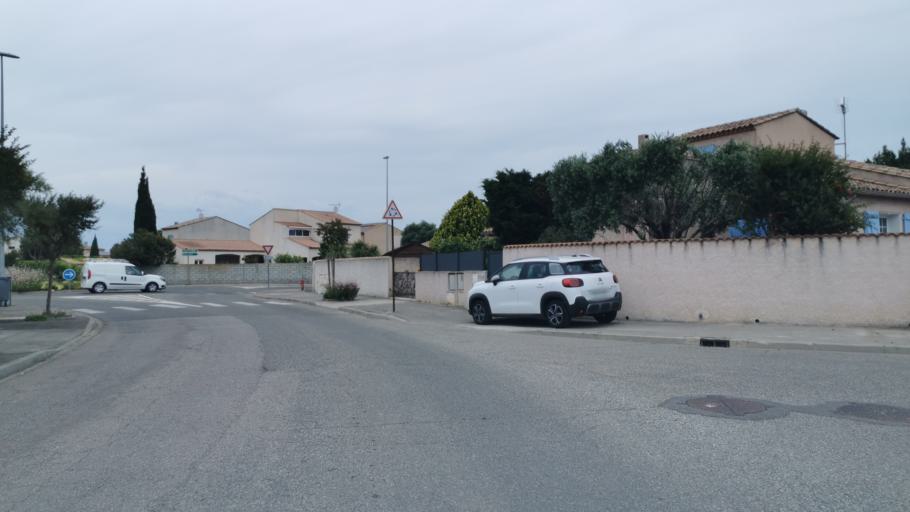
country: FR
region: Languedoc-Roussillon
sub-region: Departement de l'Aude
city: Narbonne
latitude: 43.1959
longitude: 3.0220
